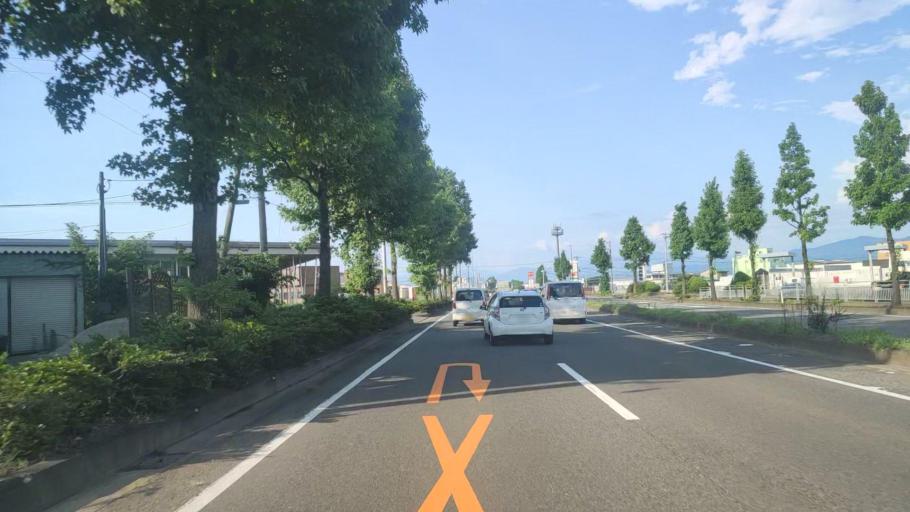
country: JP
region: Fukui
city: Fukui-shi
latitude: 36.0192
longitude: 136.2124
